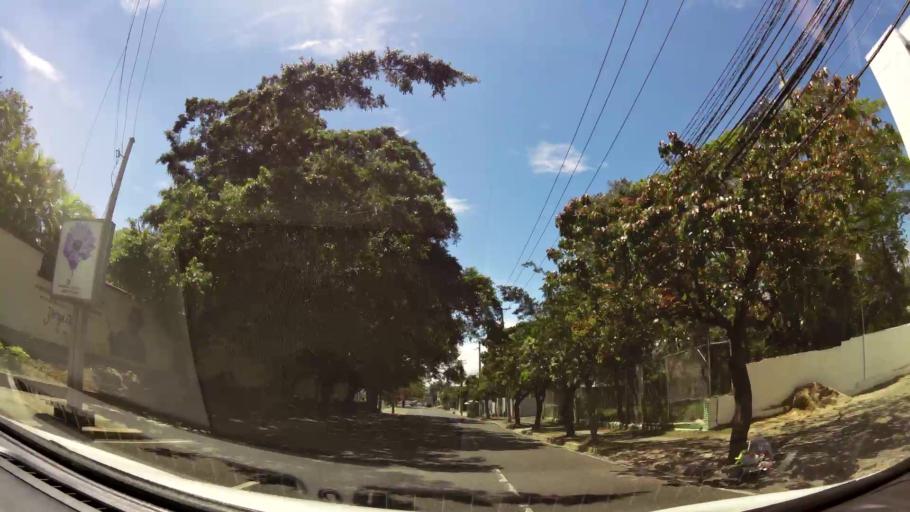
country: DO
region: Santiago
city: Santiago de los Caballeros
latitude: 19.4563
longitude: -70.6940
